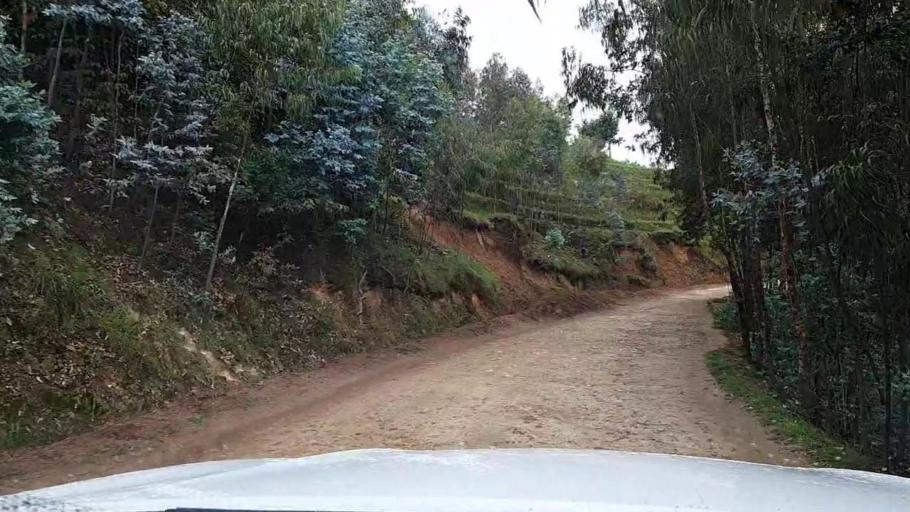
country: RW
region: Southern Province
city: Nzega
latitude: -2.4560
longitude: 29.4939
